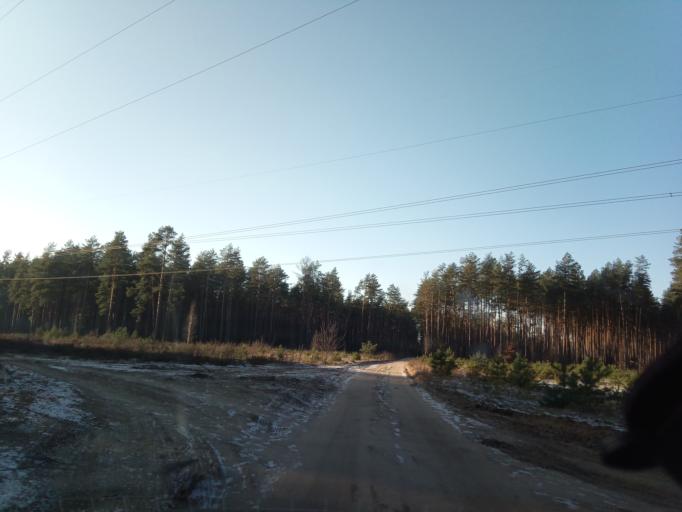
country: LT
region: Alytaus apskritis
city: Druskininkai
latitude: 53.9571
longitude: 23.8644
